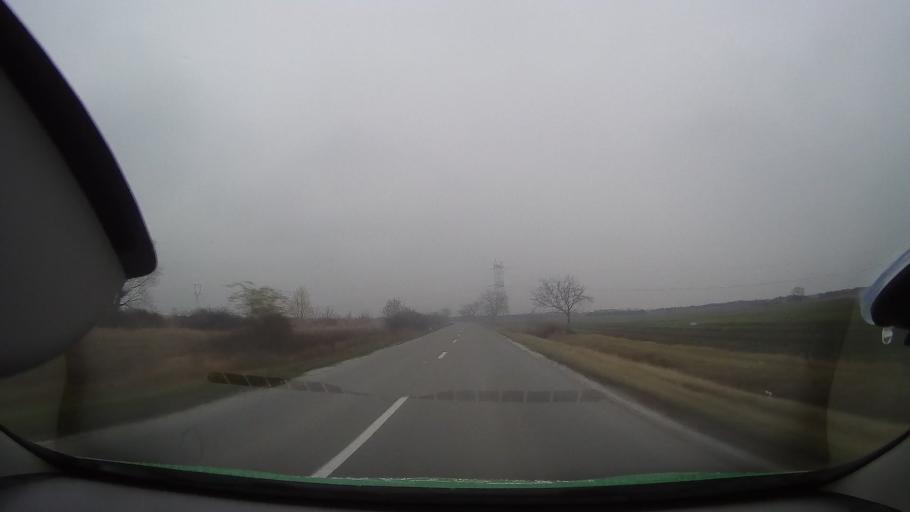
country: RO
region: Bihor
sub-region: Municipiul Salonta
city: Salonta
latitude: 46.7933
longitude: 21.6882
